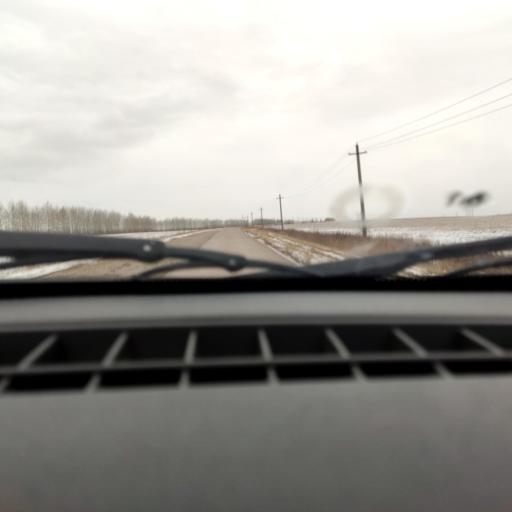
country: RU
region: Bashkortostan
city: Tolbazy
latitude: 54.2503
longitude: 55.9070
